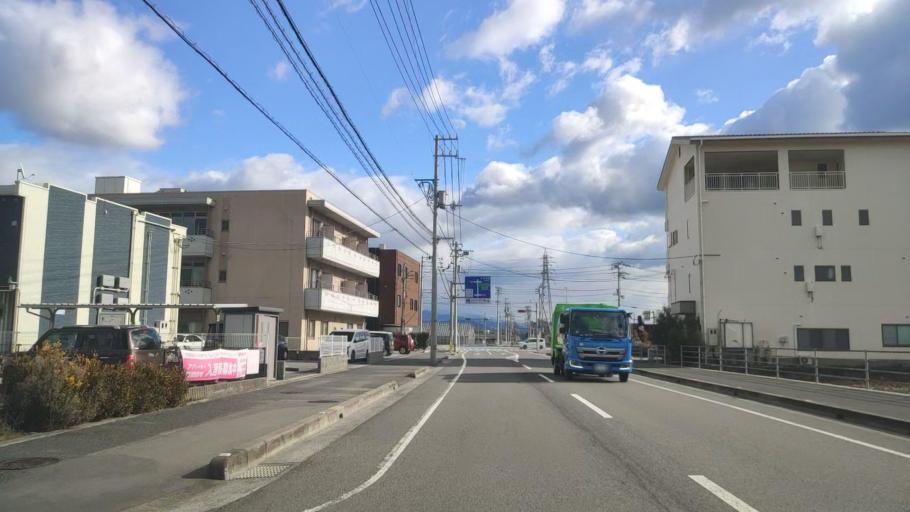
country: JP
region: Ehime
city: Masaki-cho
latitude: 33.8174
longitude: 132.7180
